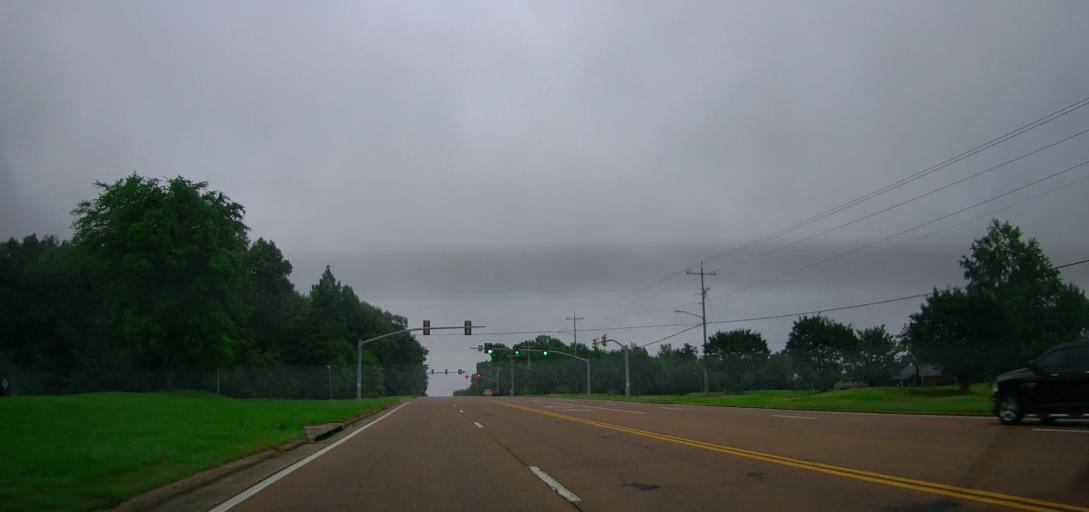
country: US
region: Mississippi
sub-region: De Soto County
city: Olive Branch
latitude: 34.9752
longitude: -89.8306
